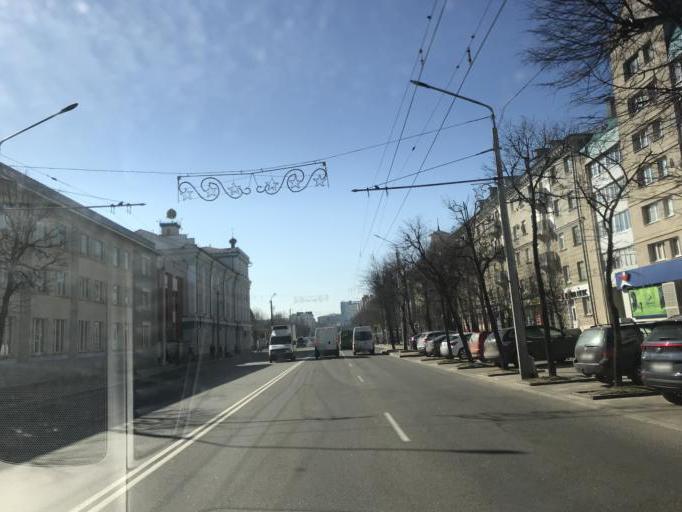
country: BY
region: Mogilev
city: Mahilyow
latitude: 53.9129
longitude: 30.3413
